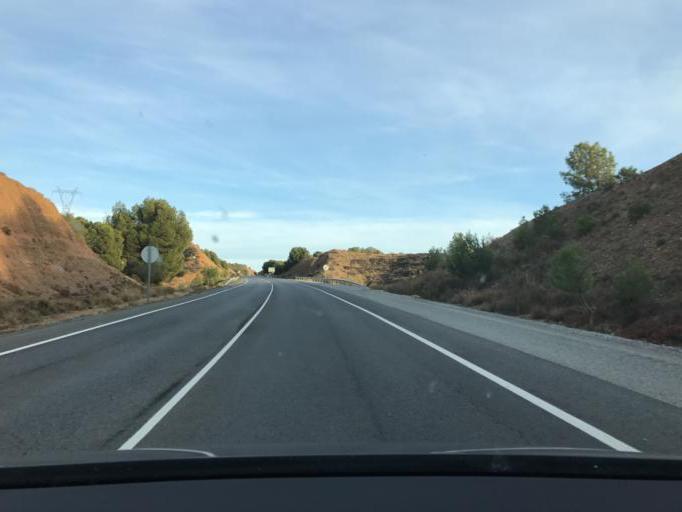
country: ES
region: Andalusia
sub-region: Provincia de Granada
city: Guadix
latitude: 37.2722
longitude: -3.1059
